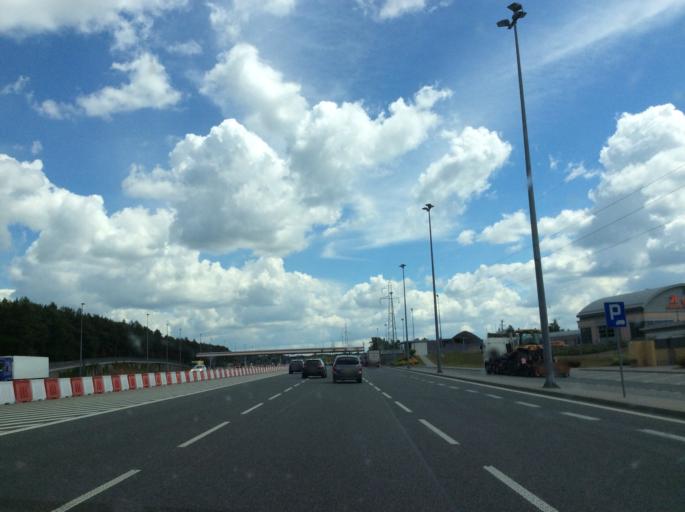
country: PL
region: Greater Poland Voivodeship
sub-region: Powiat koninski
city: Stare Miasto
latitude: 52.1535
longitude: 18.2741
